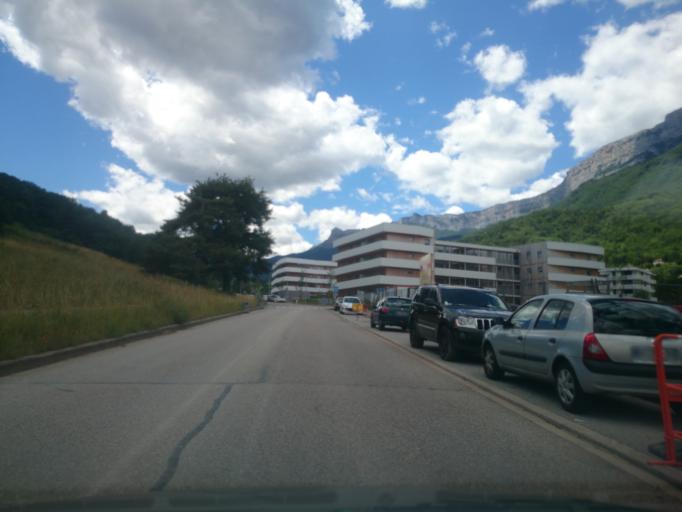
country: FR
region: Rhone-Alpes
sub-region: Departement de l'Isere
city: Seyssins
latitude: 45.1530
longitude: 5.6832
